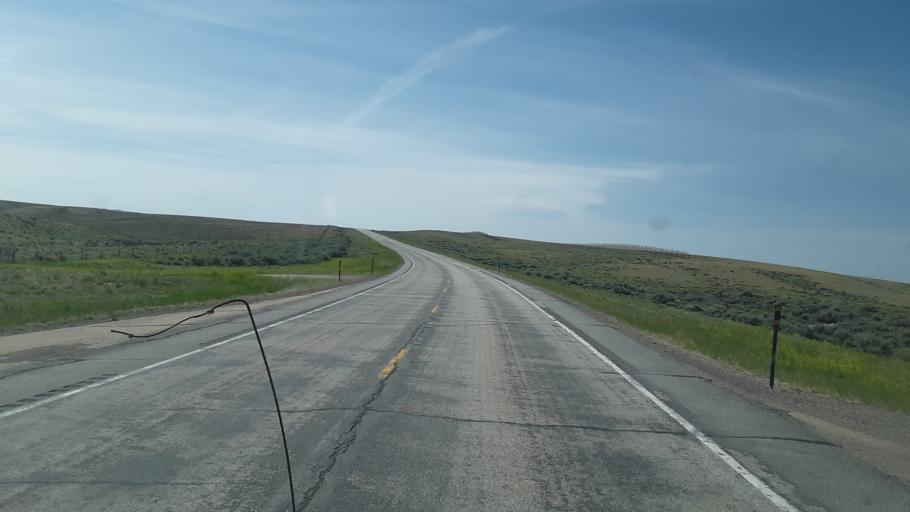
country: US
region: Wyoming
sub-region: Carbon County
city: Saratoga
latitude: 41.7117
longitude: -106.8230
